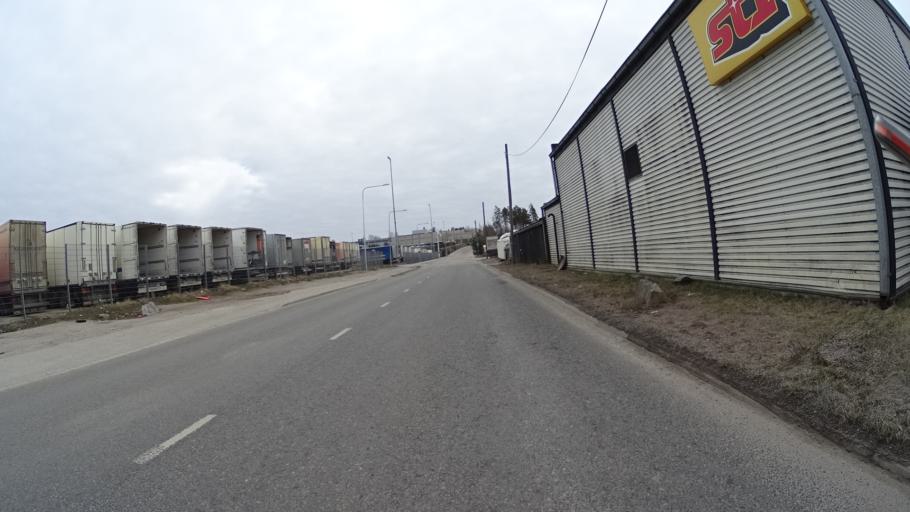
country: FI
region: Uusimaa
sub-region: Helsinki
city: Teekkarikylae
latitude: 60.2995
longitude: 24.9049
